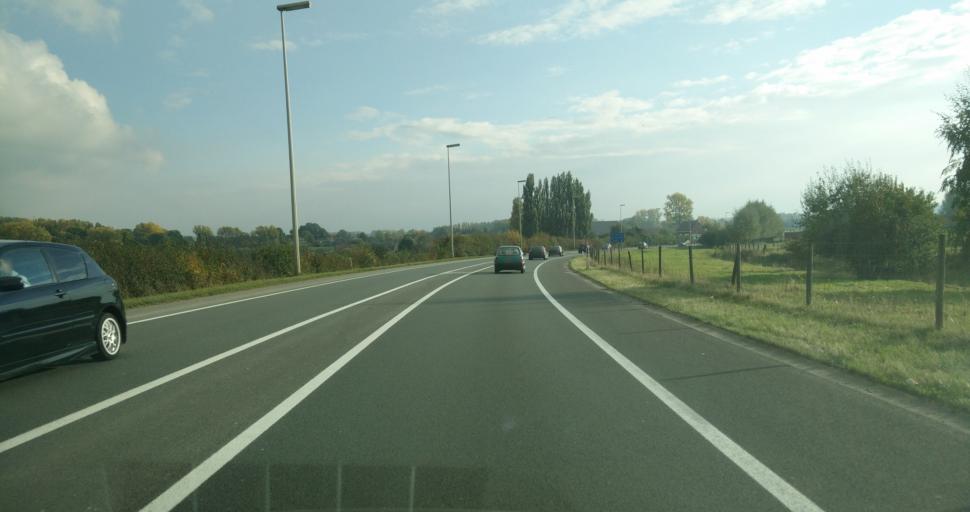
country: BE
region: Flanders
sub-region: Provincie Oost-Vlaanderen
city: Oosterzele
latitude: 50.9461
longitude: 3.8222
